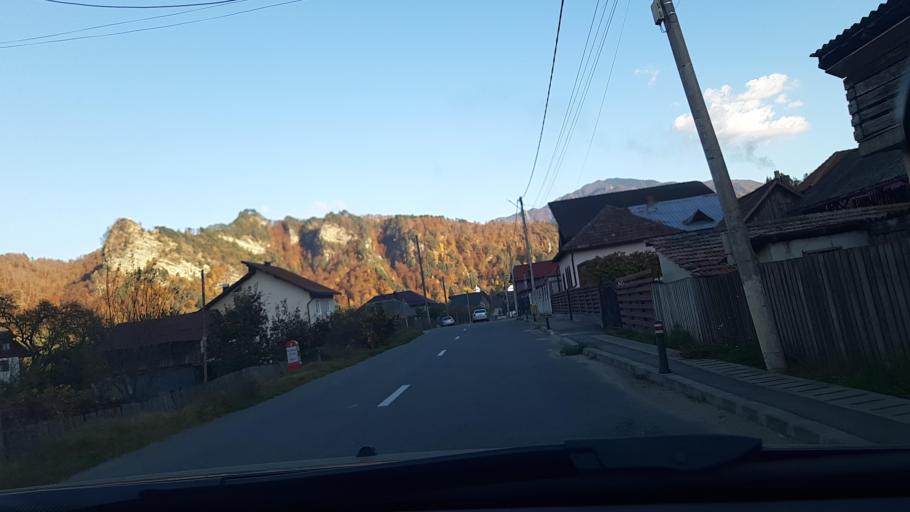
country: RO
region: Valcea
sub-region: Comuna Brezoi
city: Brezoi
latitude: 45.3444
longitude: 24.2326
